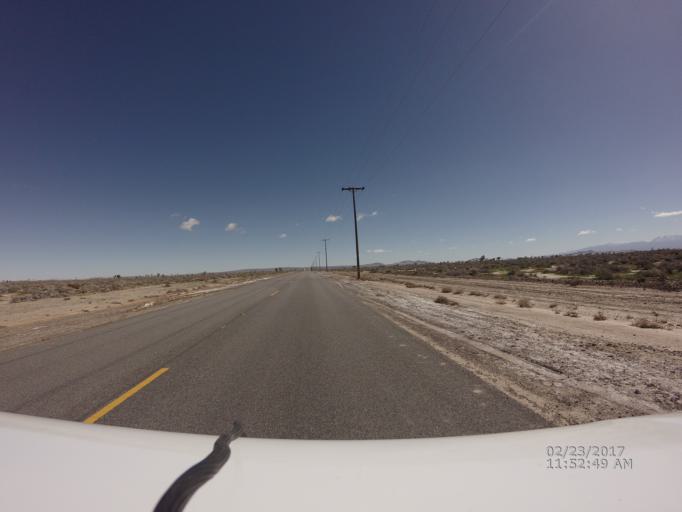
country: US
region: California
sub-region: Los Angeles County
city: Lancaster
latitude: 34.7341
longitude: -117.9960
